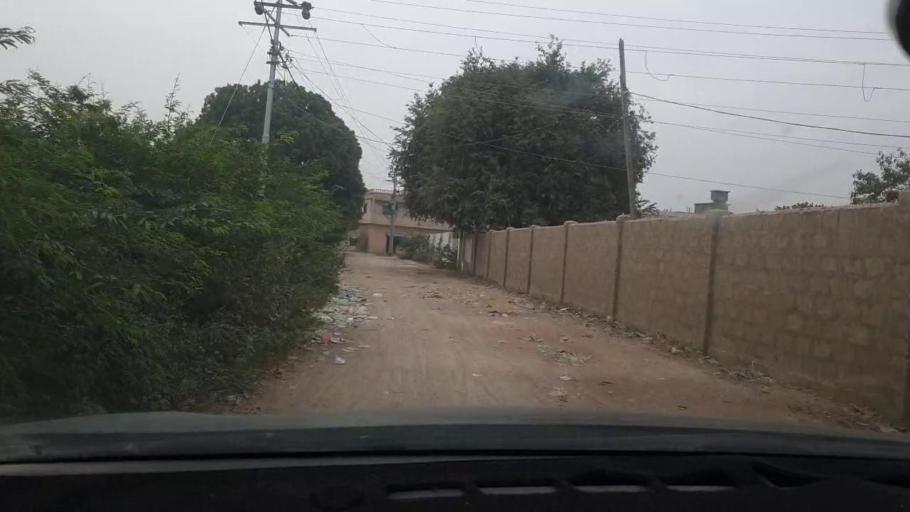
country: PK
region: Sindh
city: Malir Cantonment
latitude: 24.9218
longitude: 67.3186
